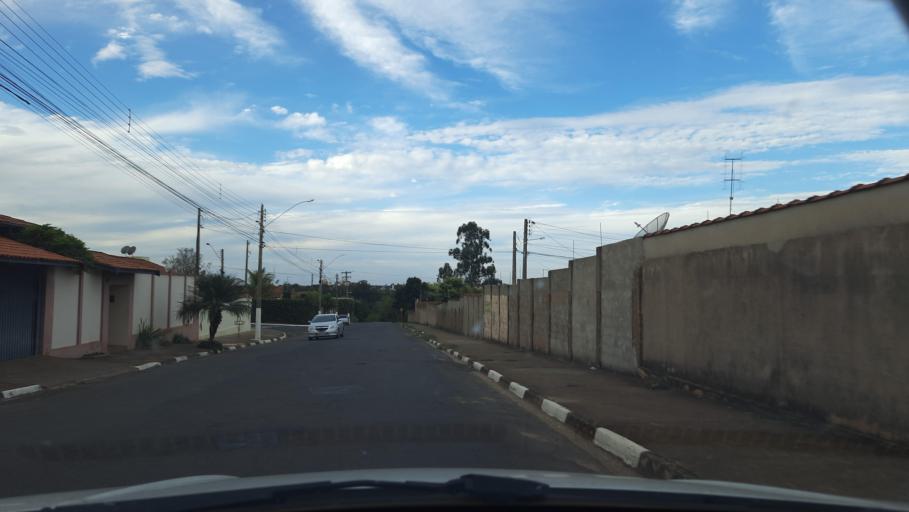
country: BR
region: Sao Paulo
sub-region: Casa Branca
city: Casa Branca
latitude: -21.7858
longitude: -47.0899
